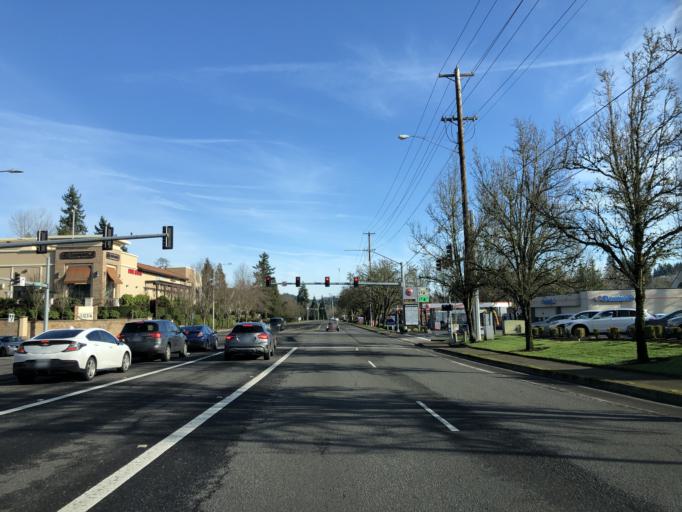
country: US
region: Oregon
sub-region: Washington County
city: Tualatin
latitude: 45.3828
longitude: -122.7491
